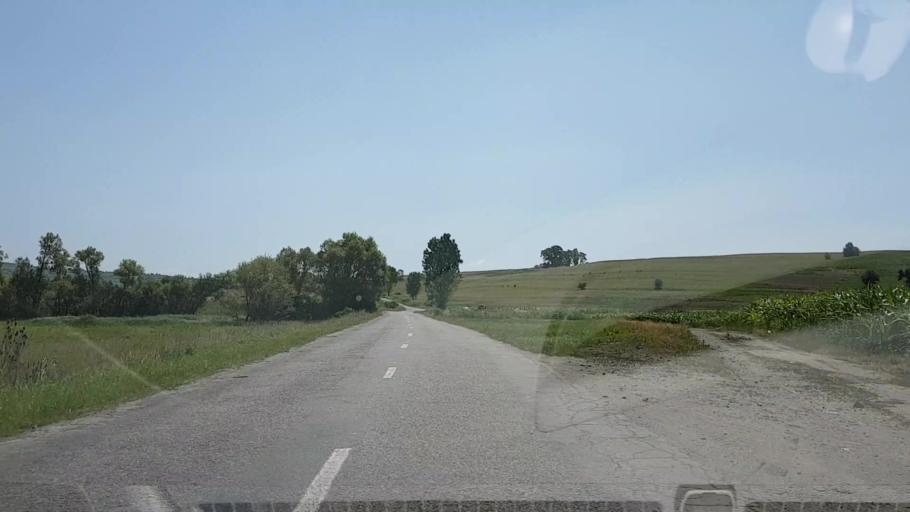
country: RO
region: Sibiu
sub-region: Comuna Merghindeal
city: Merghindeal
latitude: 45.9576
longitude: 24.7624
